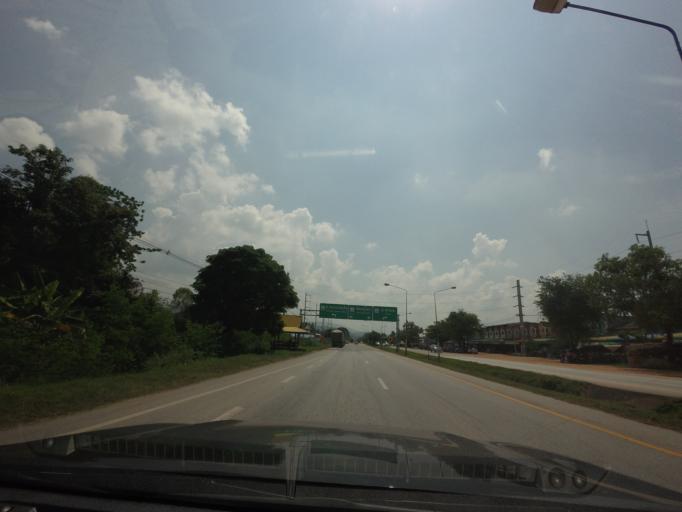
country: TH
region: Uttaradit
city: Thong Saen Khan
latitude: 17.4739
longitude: 100.2360
